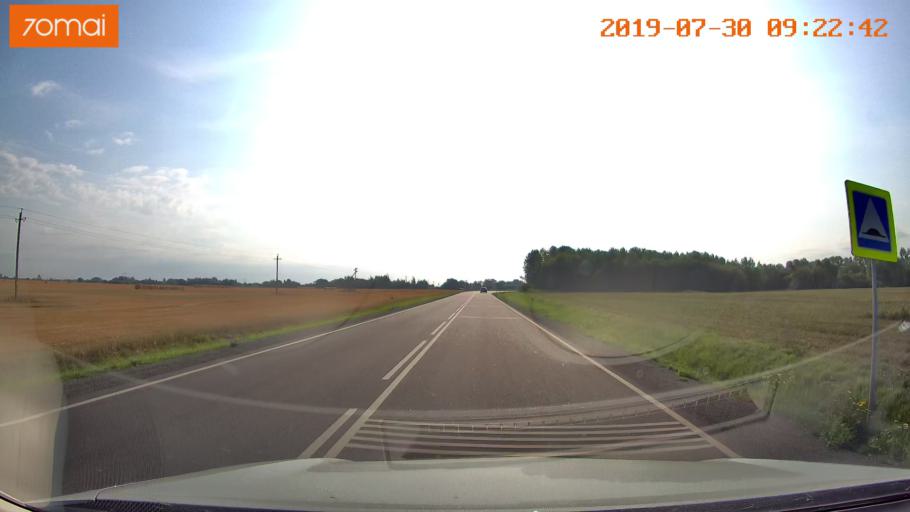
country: RU
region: Kaliningrad
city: Nesterov
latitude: 54.6338
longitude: 22.6604
